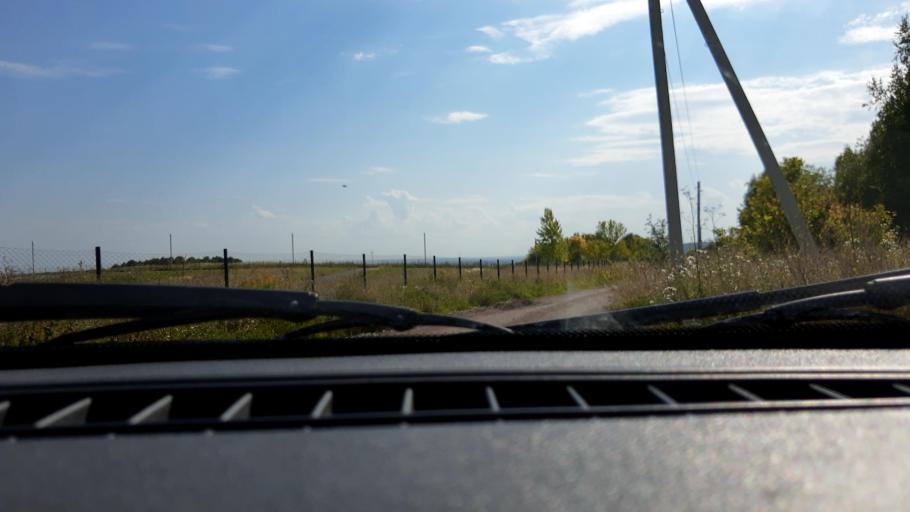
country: RU
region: Bashkortostan
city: Ufa
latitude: 54.8514
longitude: 56.1632
